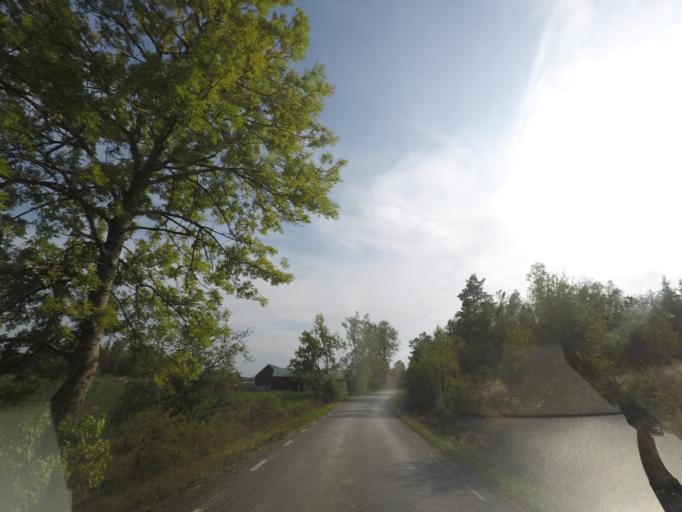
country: SE
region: Vaestmanland
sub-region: Kungsors Kommun
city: Kungsoer
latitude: 59.5069
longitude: 16.1563
